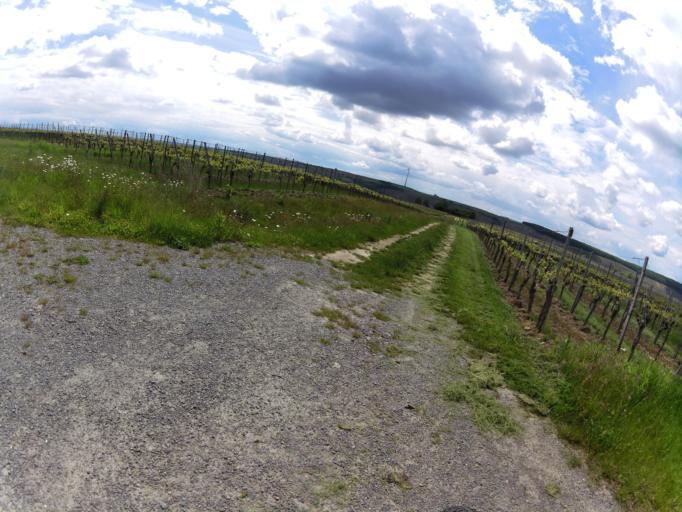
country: DE
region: Bavaria
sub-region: Regierungsbezirk Unterfranken
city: Sommerach
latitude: 49.8427
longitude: 10.1950
